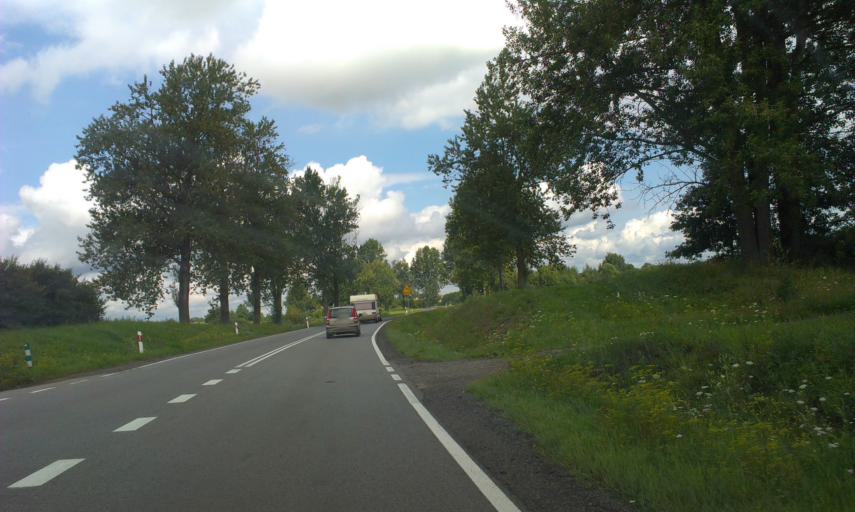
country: PL
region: West Pomeranian Voivodeship
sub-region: Powiat koszalinski
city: Bobolice
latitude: 53.9405
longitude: 16.5908
